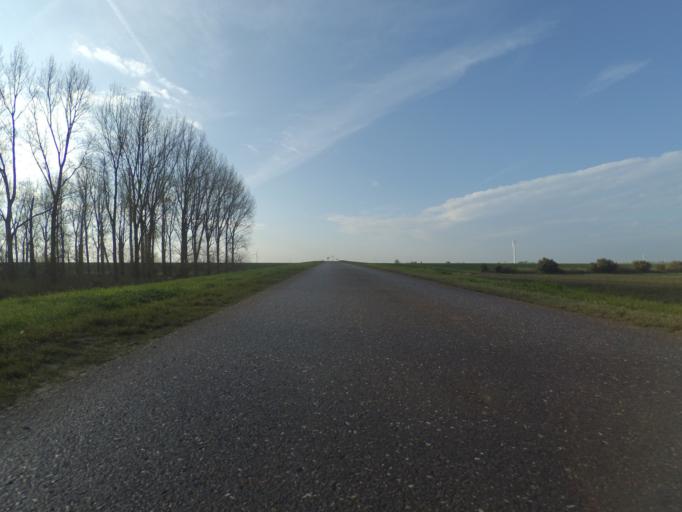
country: NL
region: Flevoland
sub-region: Gemeente Zeewolde
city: Zeewolde
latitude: 52.3719
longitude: 5.5600
